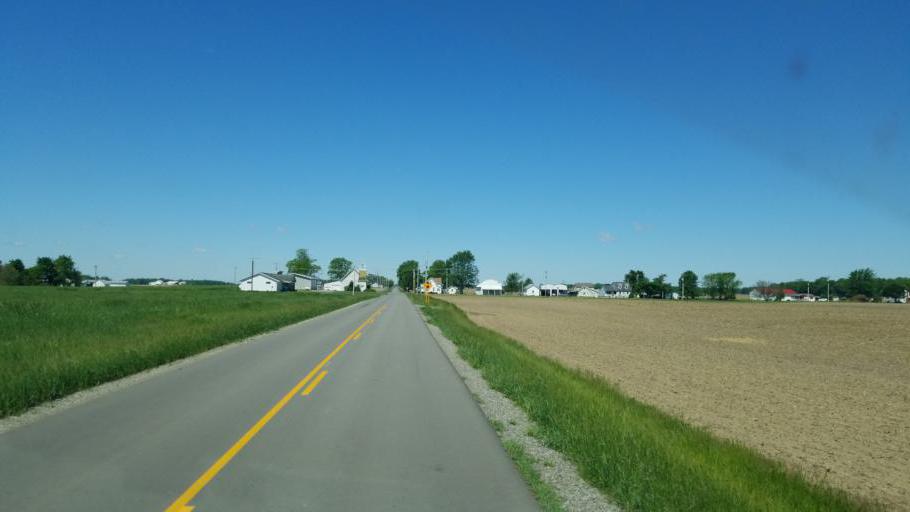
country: US
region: Ohio
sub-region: Logan County
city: Lakeview
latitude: 40.4174
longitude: -83.9424
